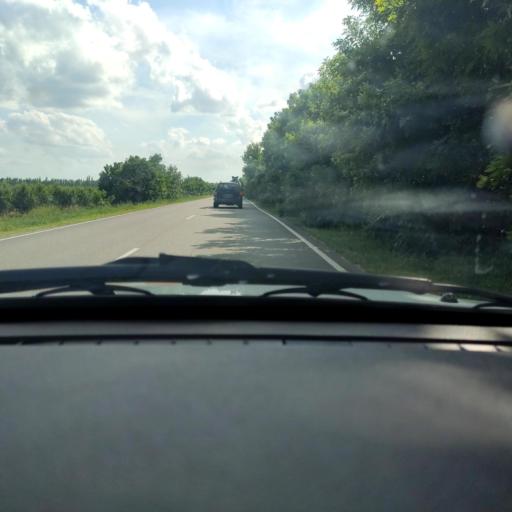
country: RU
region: Voronezj
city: Volya
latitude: 51.6963
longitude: 39.5067
